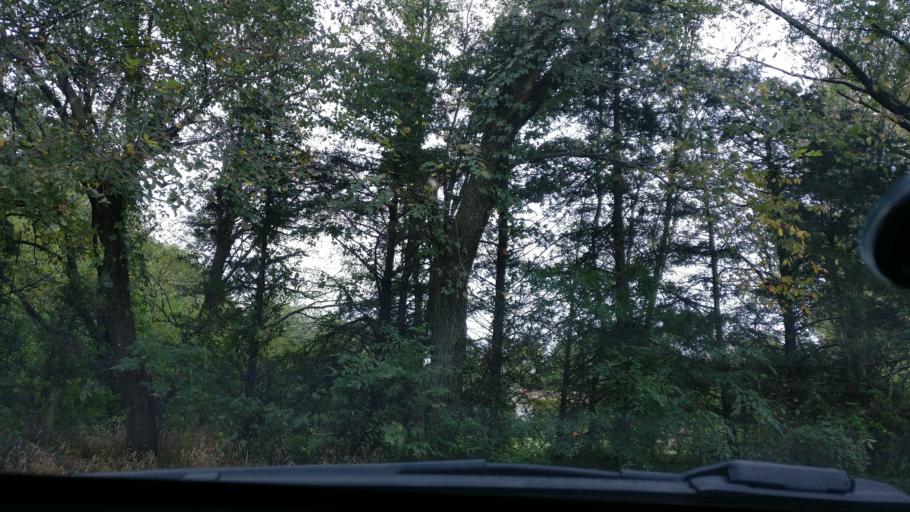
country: US
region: Oklahoma
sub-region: McClain County
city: Goldsby
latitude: 35.1896
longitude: -97.5363
